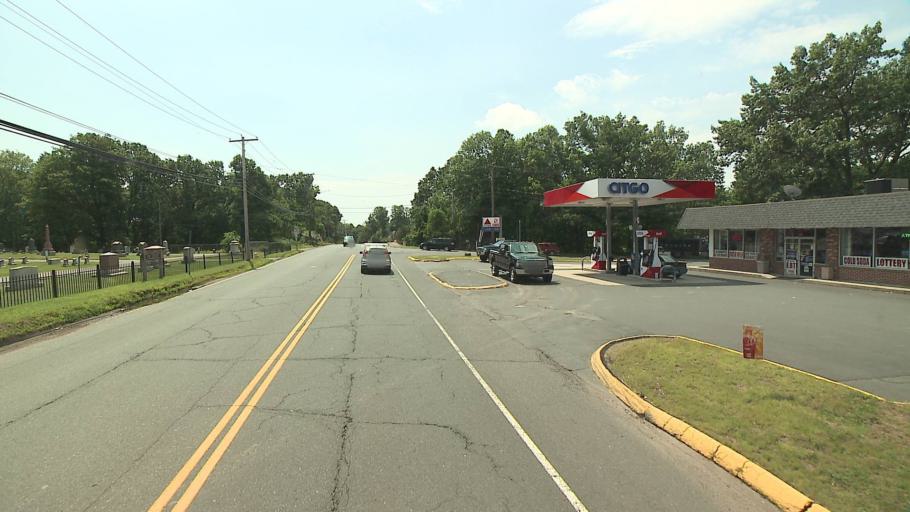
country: US
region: Connecticut
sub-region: Hartford County
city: Plainville
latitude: 41.6757
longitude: -72.8768
